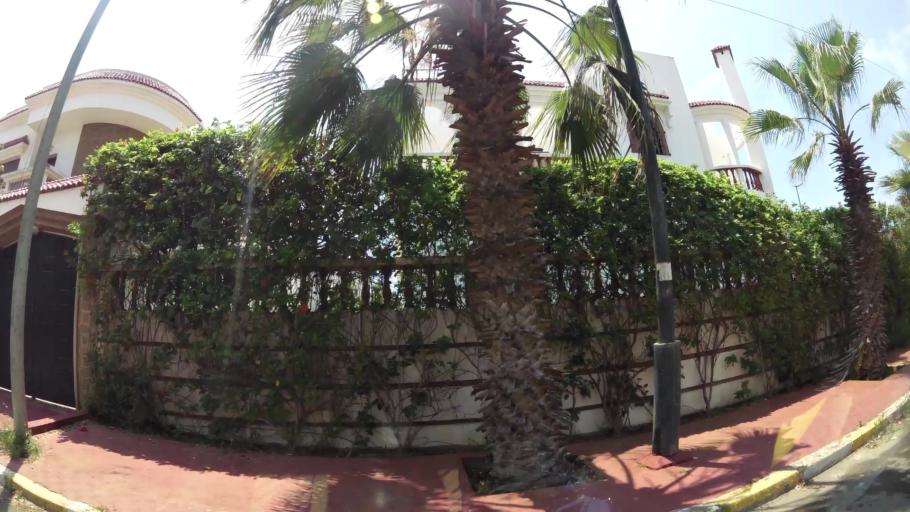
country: MA
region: Rabat-Sale-Zemmour-Zaer
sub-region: Skhirate-Temara
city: Temara
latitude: 33.9707
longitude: -6.9022
